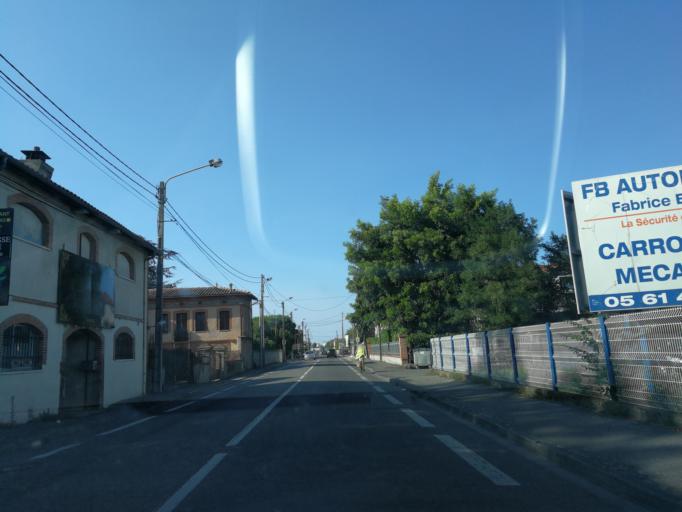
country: FR
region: Midi-Pyrenees
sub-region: Departement de la Haute-Garonne
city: Aucamville
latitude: 43.6434
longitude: 1.4392
